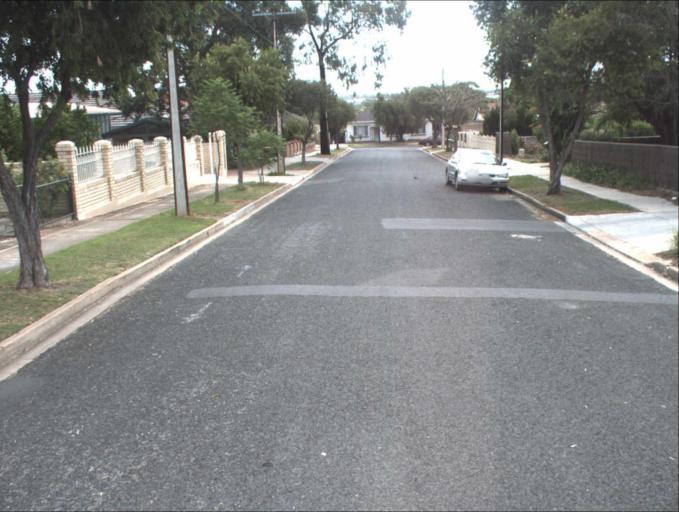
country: AU
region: South Australia
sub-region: Port Adelaide Enfield
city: Blair Athol
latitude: -34.8646
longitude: 138.5984
